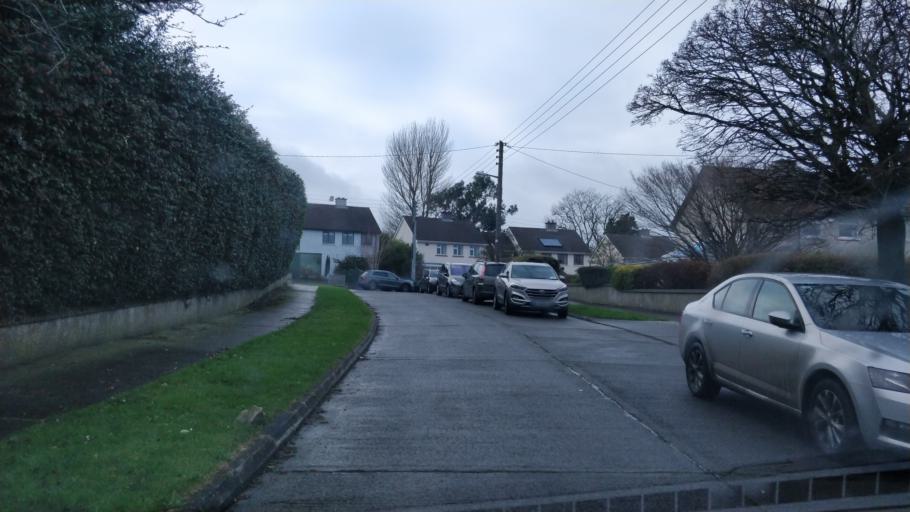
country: IE
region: Leinster
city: Foxrock
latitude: 53.2819
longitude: -6.1763
